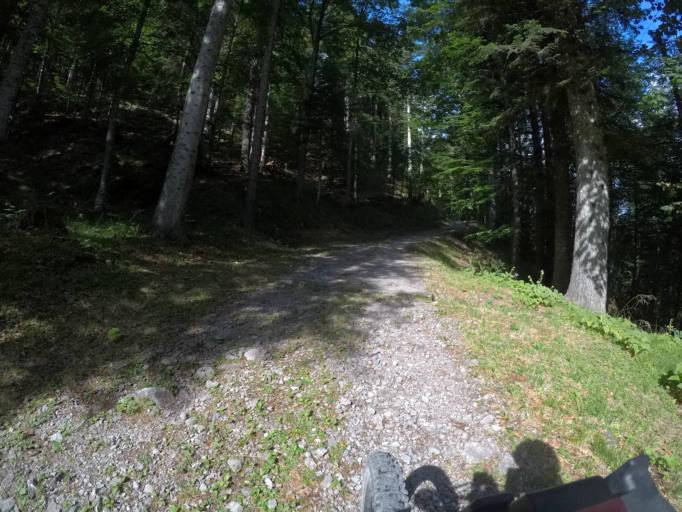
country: IT
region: Friuli Venezia Giulia
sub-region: Provincia di Udine
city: Paularo
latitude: 46.4987
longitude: 13.1732
